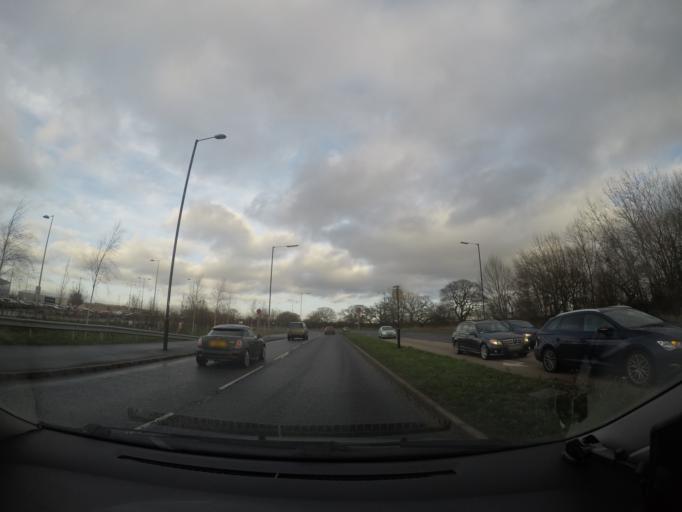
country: GB
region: England
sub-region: City of York
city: Huntington
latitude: 53.9821
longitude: -1.0460
